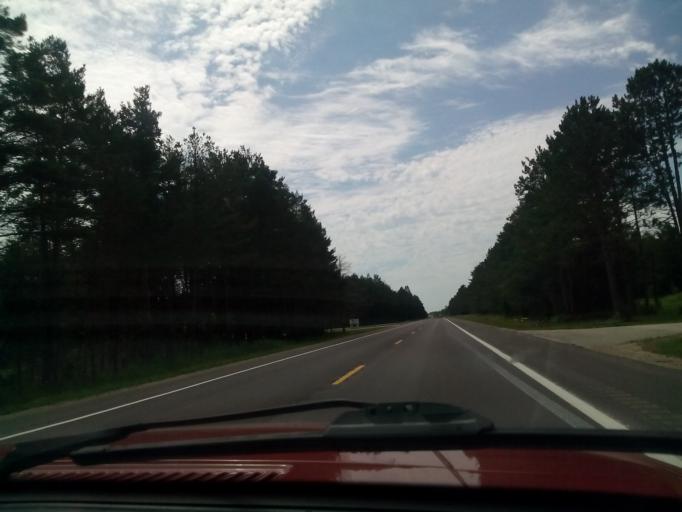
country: US
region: Michigan
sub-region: Schoolcraft County
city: Manistique
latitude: 46.0489
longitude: -85.9667
